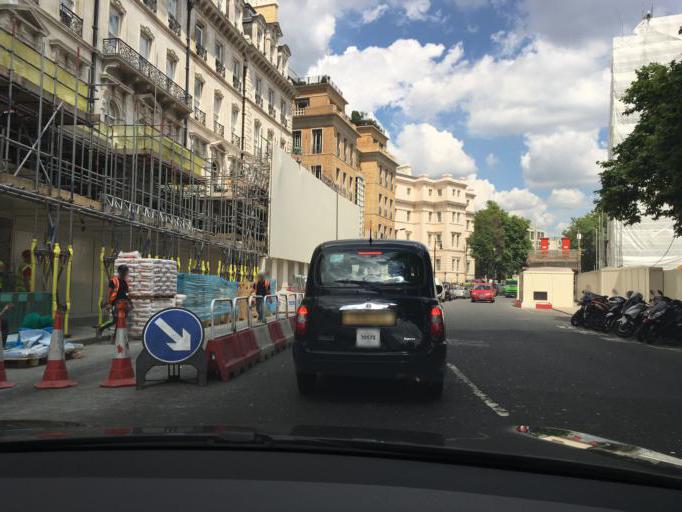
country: GB
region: England
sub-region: Greater London
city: Chelsea
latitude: 51.5012
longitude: -0.1534
